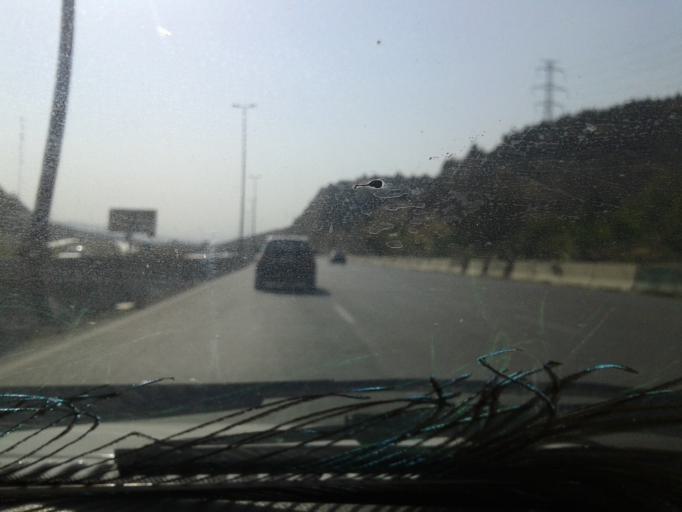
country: IR
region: Tehran
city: Tehran
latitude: 35.7332
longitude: 51.6579
